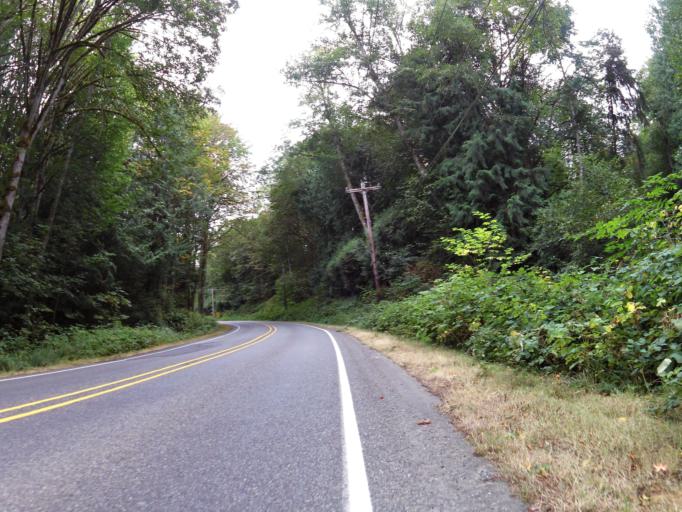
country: US
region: Washington
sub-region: Jefferson County
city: Port Ludlow
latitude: 47.9561
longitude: -122.6981
